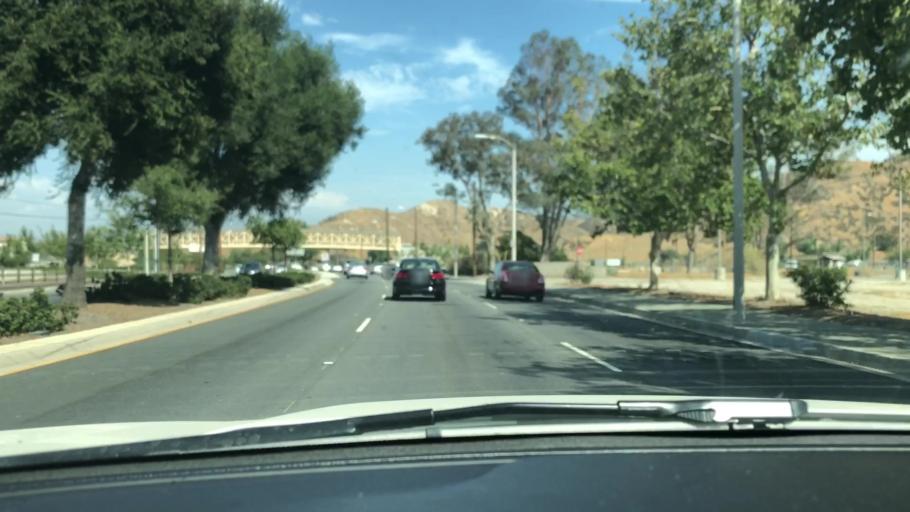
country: US
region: California
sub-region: Los Angeles County
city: Santa Clarita
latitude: 34.4151
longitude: -118.5242
